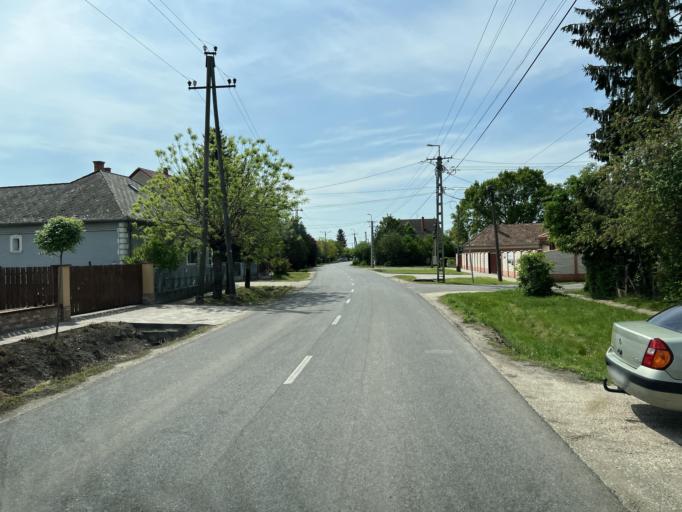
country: HU
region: Pest
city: Abony
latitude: 47.1983
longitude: 20.0130
